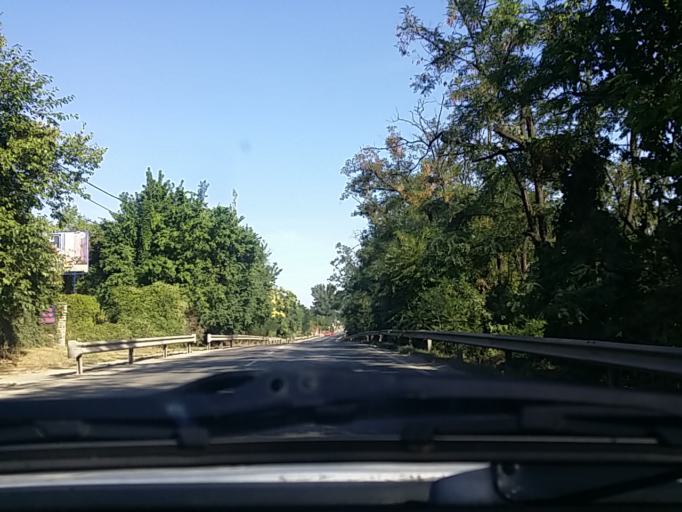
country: HU
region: Pest
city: Urom
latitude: 47.5800
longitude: 19.0049
